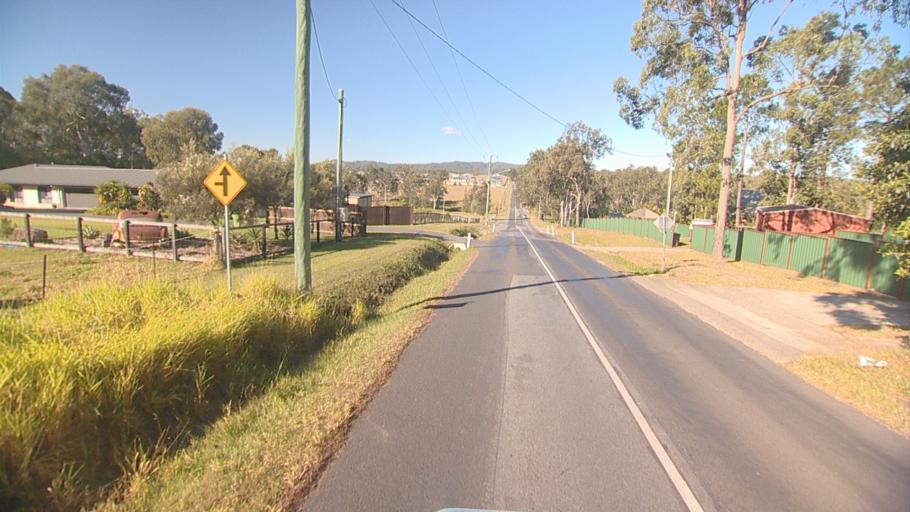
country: AU
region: Queensland
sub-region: Logan
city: Chambers Flat
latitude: -27.7771
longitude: 153.0906
